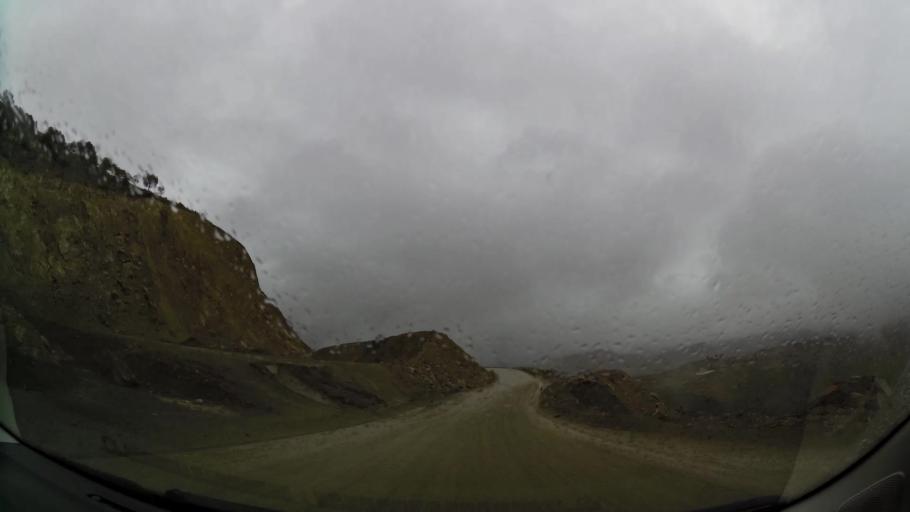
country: MA
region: Oriental
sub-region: Nador
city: Midar
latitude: 34.8974
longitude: -3.7783
